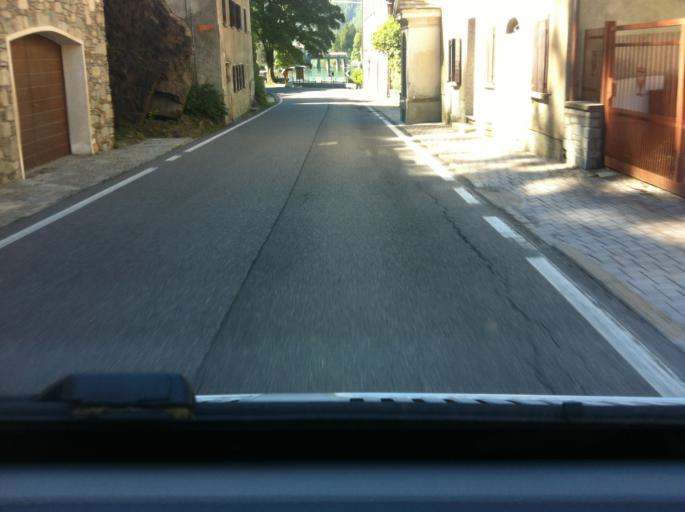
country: IT
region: Lombardy
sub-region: Provincia di Sondrio
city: Campodolcino
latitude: 46.4166
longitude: 9.3422
